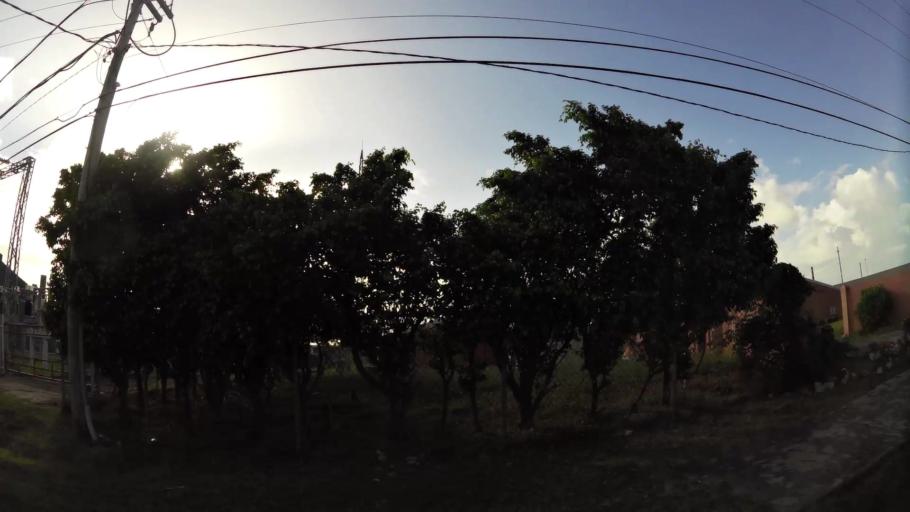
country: AG
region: Saint John
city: Saint John's
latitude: 17.1367
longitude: -61.8362
